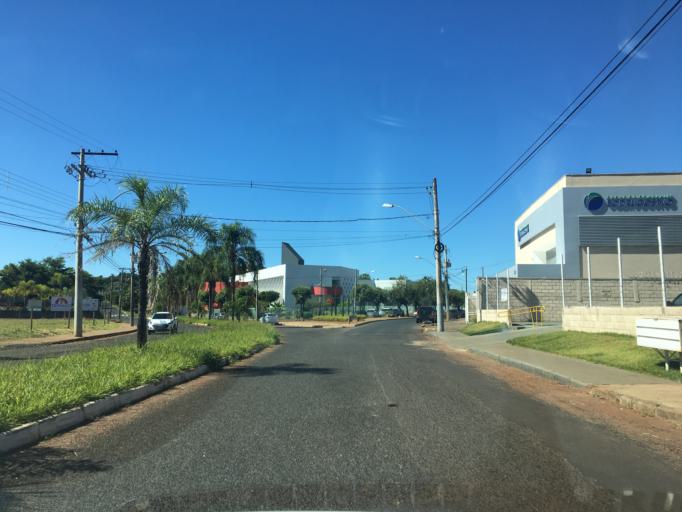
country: BR
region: Minas Gerais
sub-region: Uberlandia
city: Uberlandia
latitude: -18.9331
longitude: -48.2815
